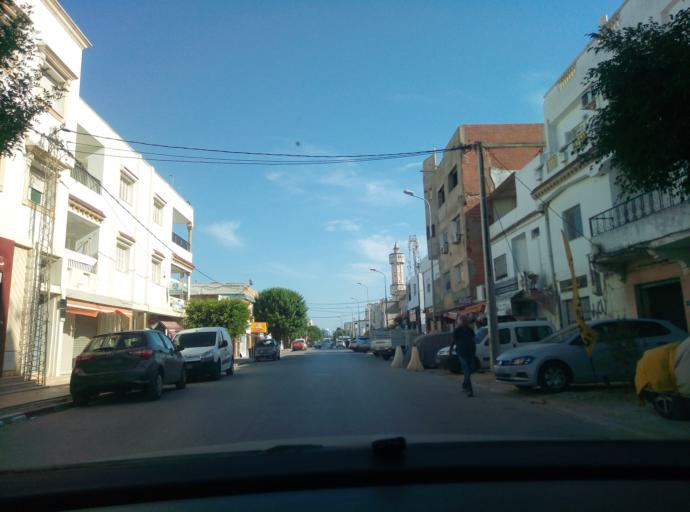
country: TN
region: Tunis
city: La Goulette
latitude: 36.8530
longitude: 10.2614
